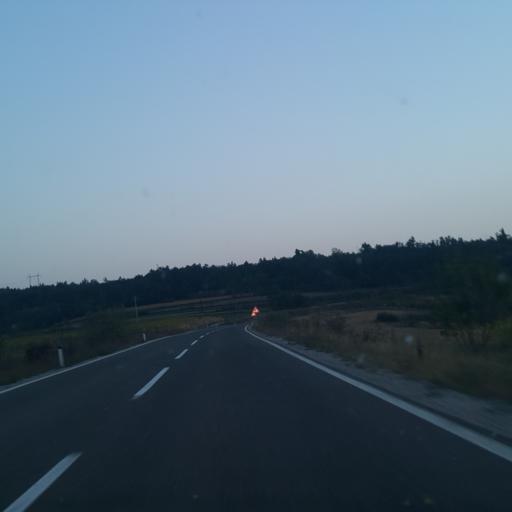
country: RS
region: Central Serbia
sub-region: Nisavski Okrug
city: Svrljig
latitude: 43.4482
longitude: 22.1711
